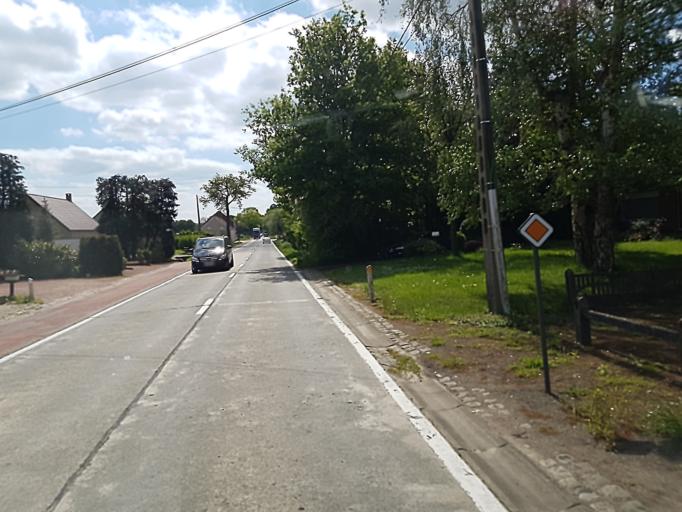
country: BE
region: Flanders
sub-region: Provincie Vlaams-Brabant
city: Scherpenheuvel-Zichem
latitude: 51.0293
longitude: 5.0144
